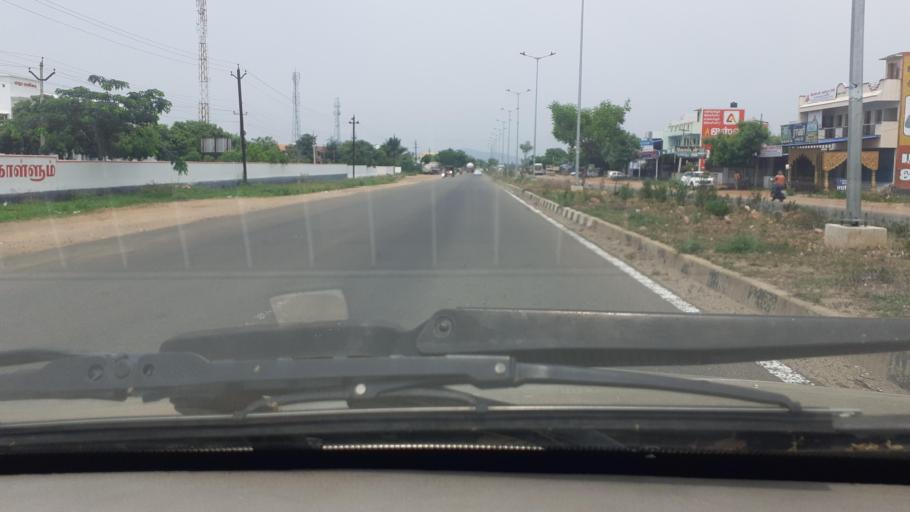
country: IN
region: Tamil Nadu
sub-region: Tirunelveli Kattabo
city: Tirunelveli
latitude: 8.7140
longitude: 77.7848
